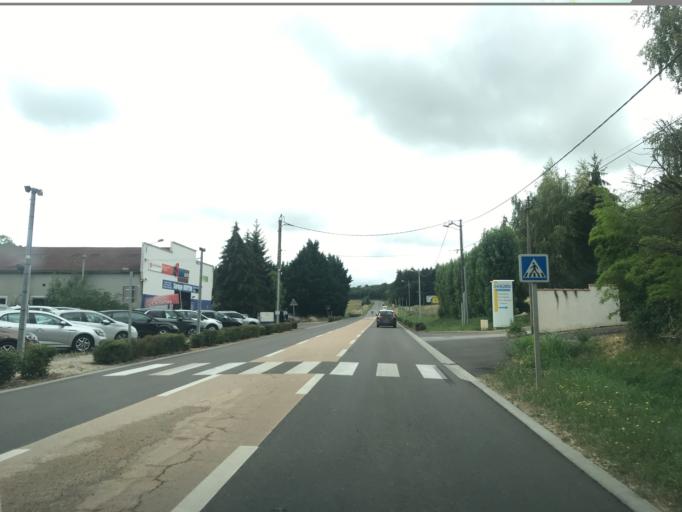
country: FR
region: Poitou-Charentes
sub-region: Departement de la Charente
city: Dignac
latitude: 45.5524
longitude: 0.2760
